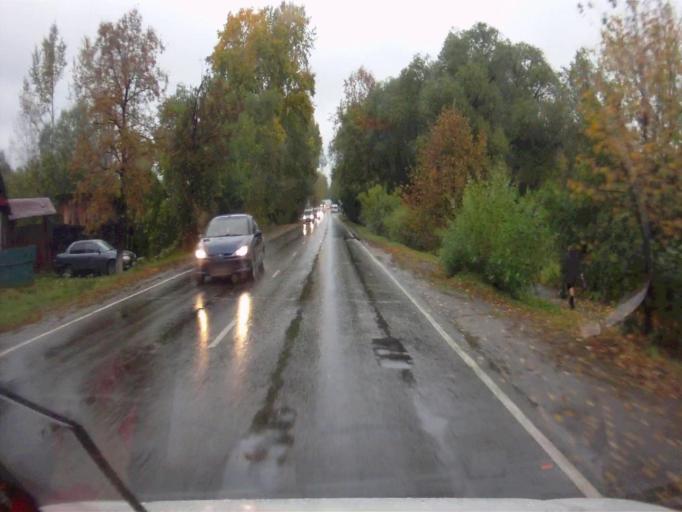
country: RU
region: Chelyabinsk
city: Kyshtym
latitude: 55.7178
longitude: 60.5421
